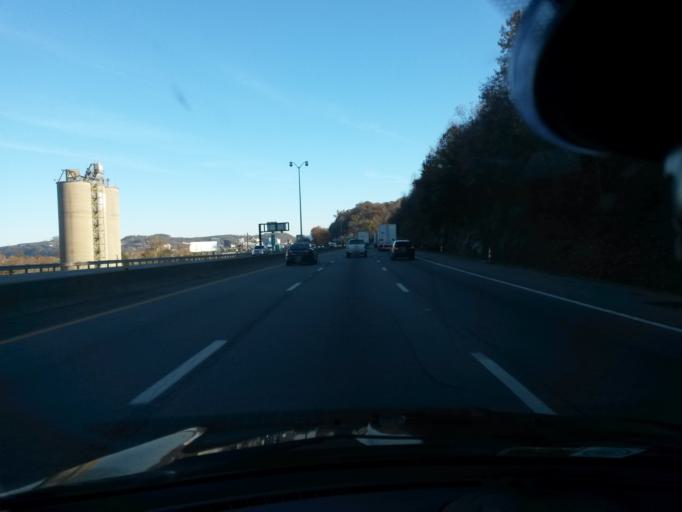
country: US
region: West Virginia
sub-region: Kanawha County
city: South Charleston
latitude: 38.3610
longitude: -81.6665
